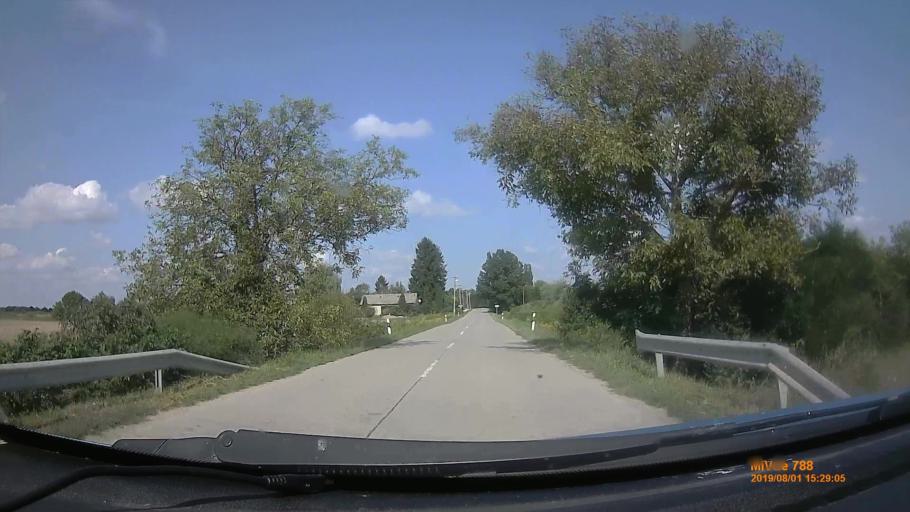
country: HU
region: Baranya
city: Sellye
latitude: 45.9216
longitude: 17.8686
